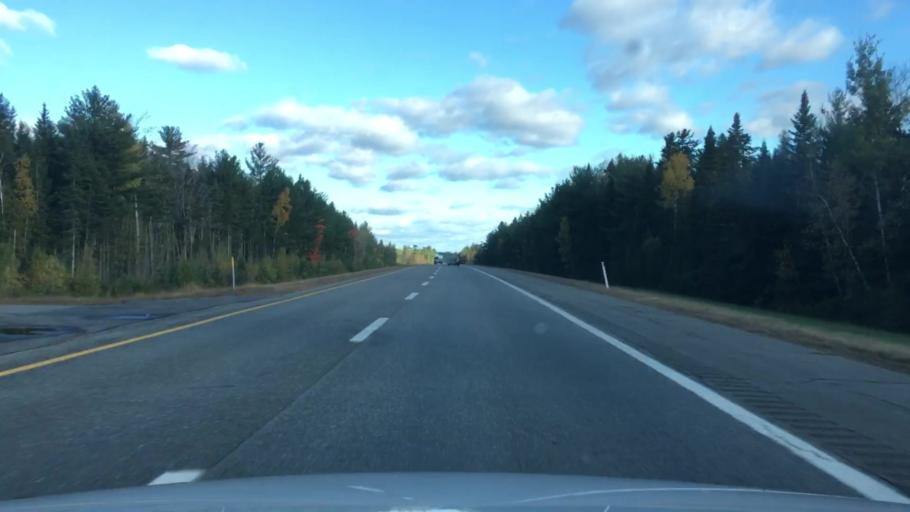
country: US
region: Maine
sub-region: Penobscot County
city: Greenbush
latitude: 45.1251
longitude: -68.6949
